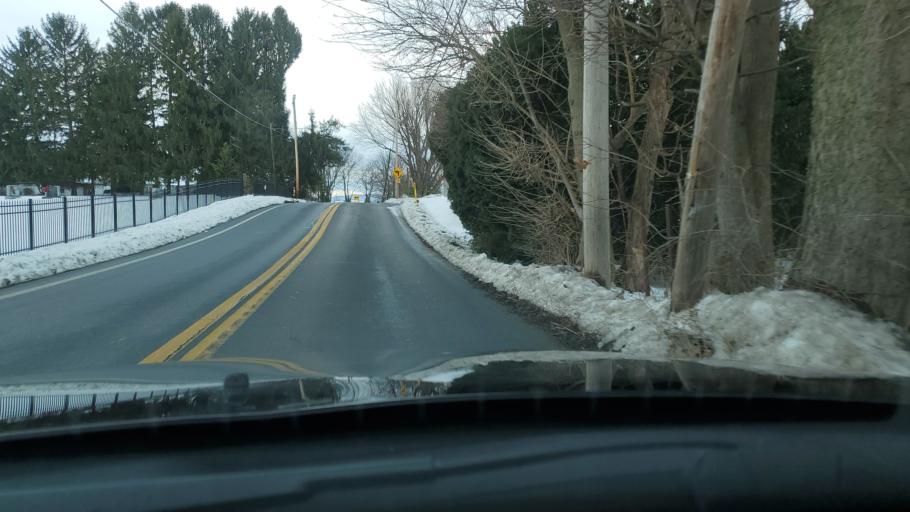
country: US
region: Pennsylvania
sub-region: Cumberland County
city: Mechanicsburg
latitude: 40.2096
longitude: -77.0314
